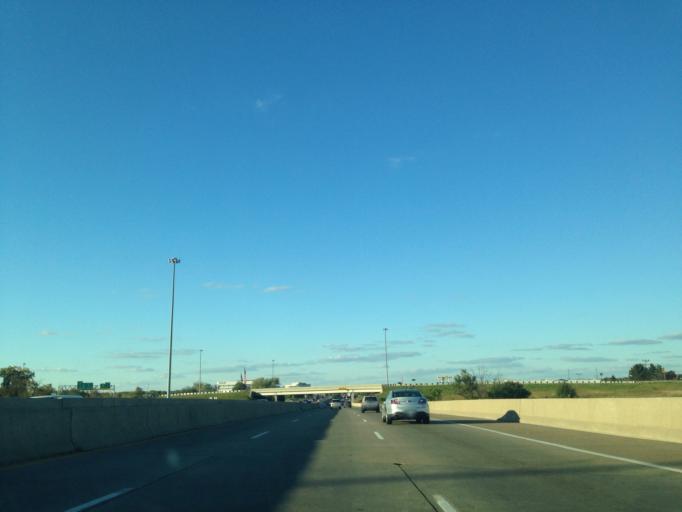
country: US
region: Michigan
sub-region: Oakland County
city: Bingham Farms
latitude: 42.4891
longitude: -83.2846
